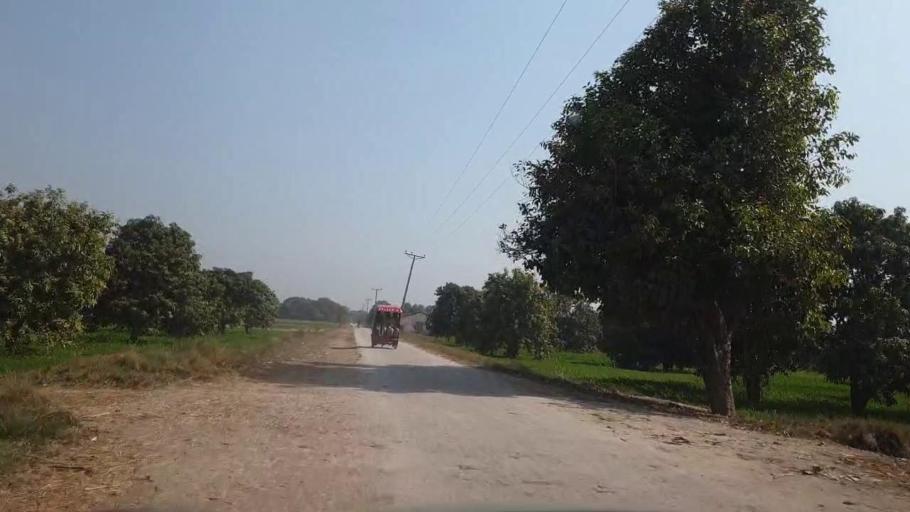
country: PK
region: Sindh
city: Tando Allahyar
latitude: 25.5384
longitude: 68.7090
